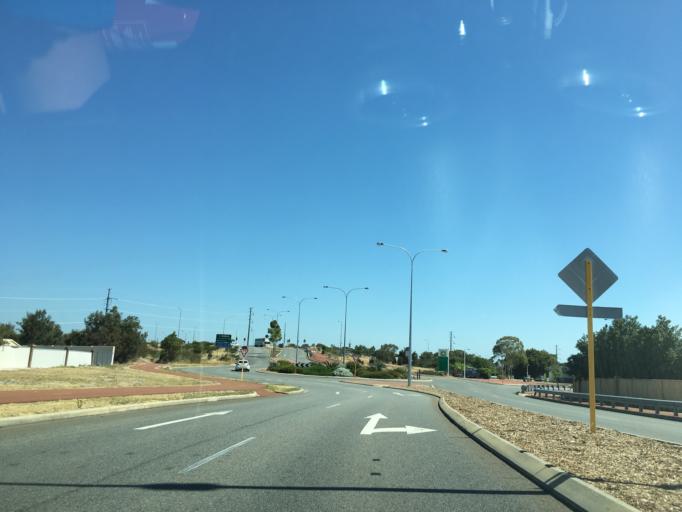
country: AU
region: Western Australia
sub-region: Canning
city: Canning Vale
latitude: -32.0543
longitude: 115.9045
